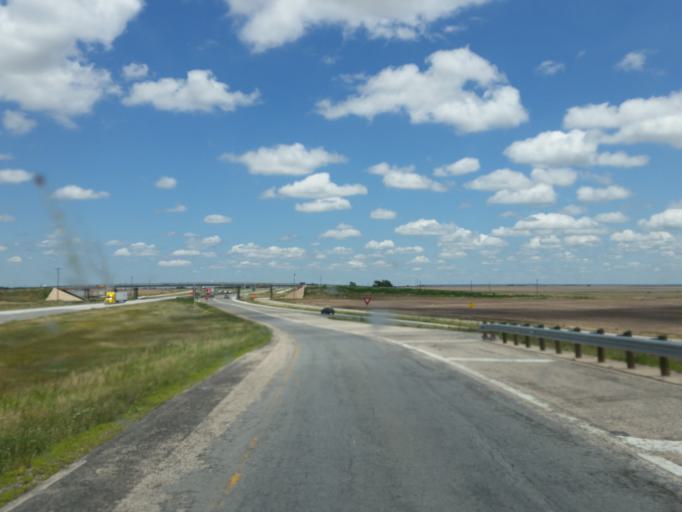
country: US
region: Texas
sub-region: Nolan County
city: Roscoe
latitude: 32.4457
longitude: -100.5064
